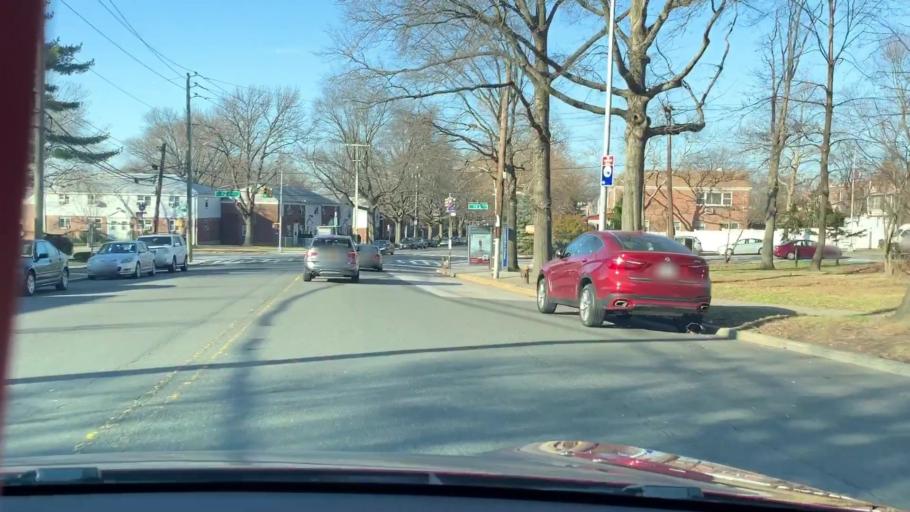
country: US
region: New York
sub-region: Nassau County
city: Bellerose Terrace
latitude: 40.7420
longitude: -73.7531
